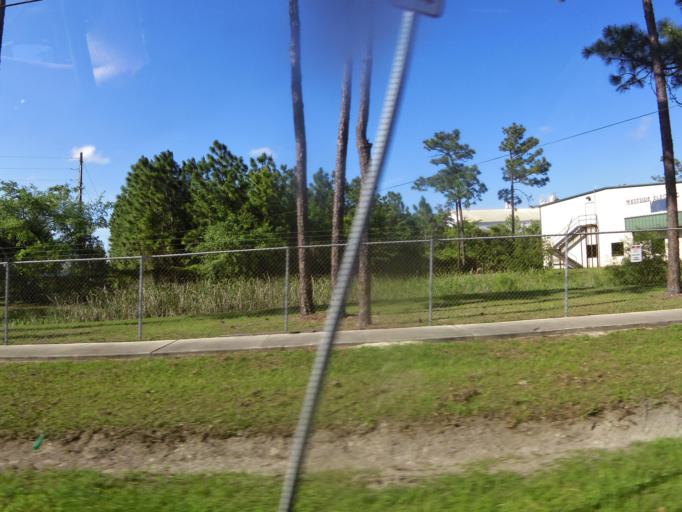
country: US
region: Florida
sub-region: Duval County
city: Jacksonville
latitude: 30.4334
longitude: -81.5607
